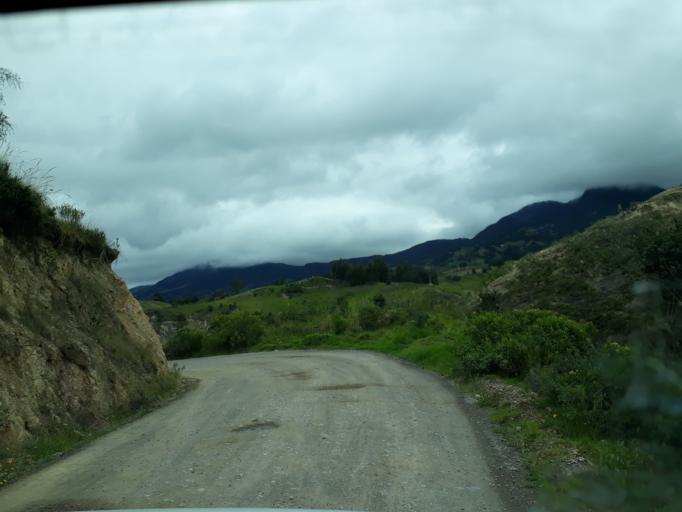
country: CO
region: Cundinamarca
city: Carmen de Carupa
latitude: 5.3173
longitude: -73.8929
